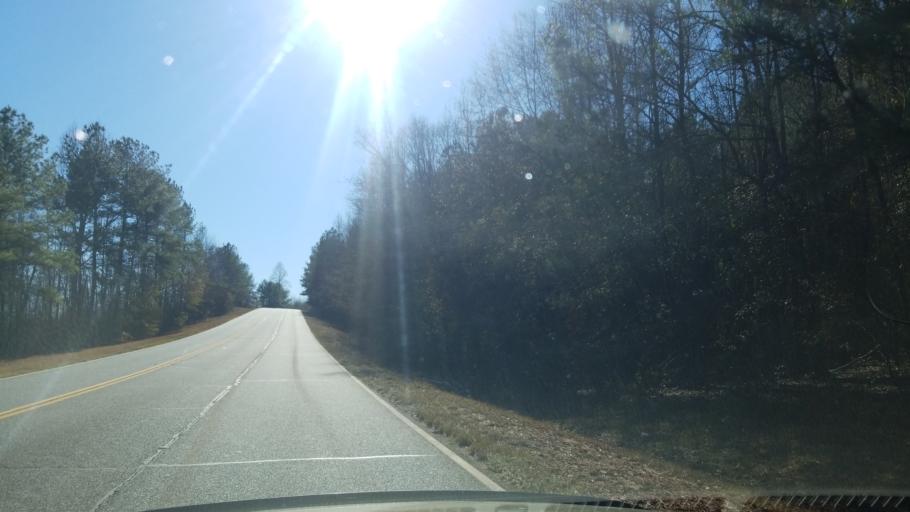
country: US
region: Georgia
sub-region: Talbot County
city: Sardis
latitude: 32.8146
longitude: -84.6472
